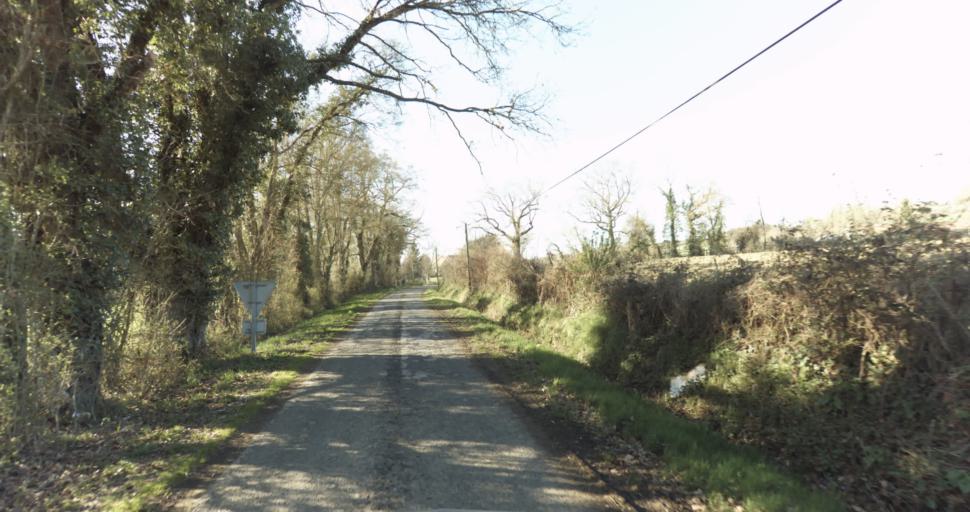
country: FR
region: Lower Normandy
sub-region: Departement du Calvados
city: Saint-Pierre-sur-Dives
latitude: 49.0452
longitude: 0.0272
